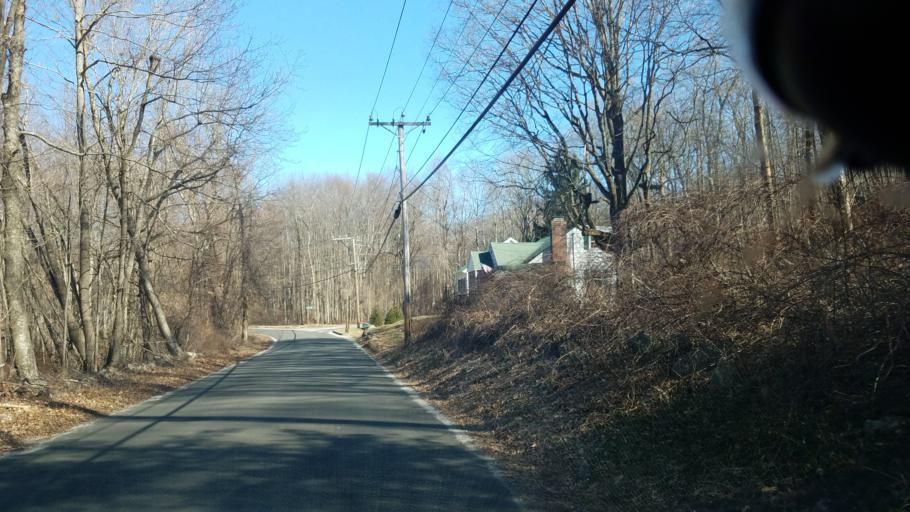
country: US
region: Connecticut
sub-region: Fairfield County
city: Newtown
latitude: 41.3527
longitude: -73.3153
